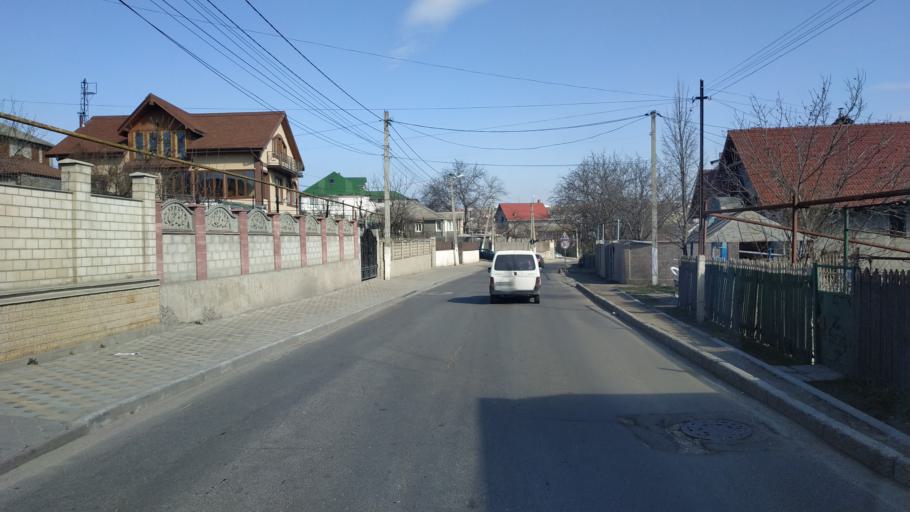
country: MD
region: Chisinau
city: Vatra
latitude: 47.0241
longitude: 28.7689
